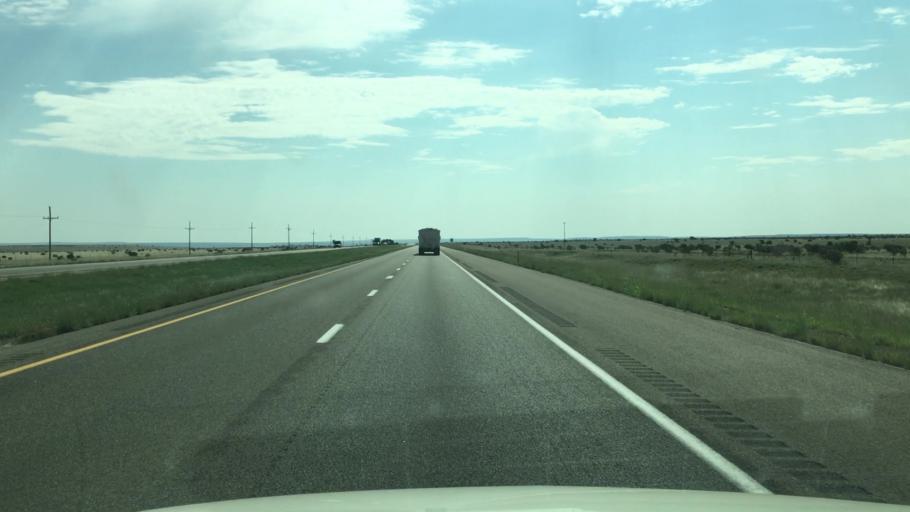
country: US
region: New Mexico
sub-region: Guadalupe County
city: Santa Rosa
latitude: 34.9826
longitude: -105.1169
